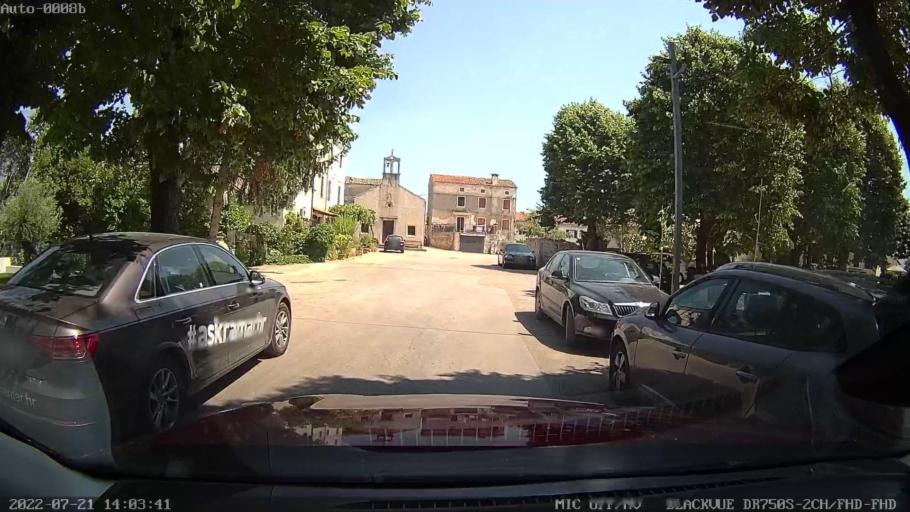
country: HR
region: Istarska
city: Vodnjan
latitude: 45.0891
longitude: 13.8827
